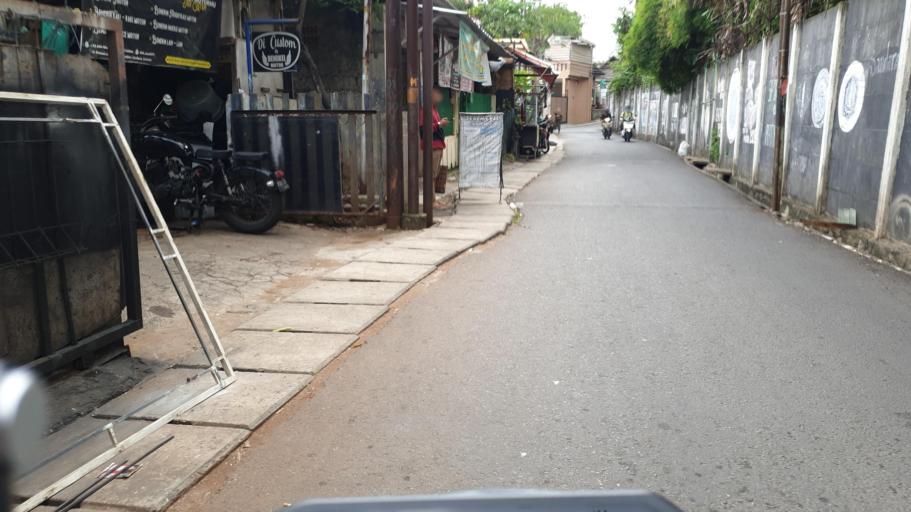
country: ID
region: Banten
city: South Tangerang
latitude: -6.2749
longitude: 106.7916
